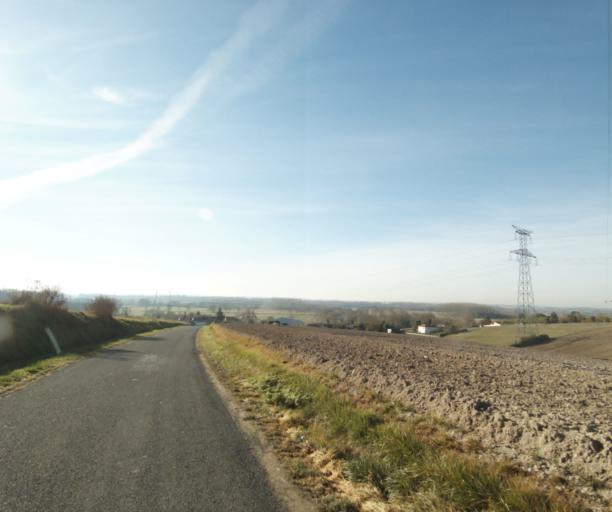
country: FR
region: Poitou-Charentes
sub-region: Departement de la Charente-Maritime
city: Chaniers
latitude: 45.7291
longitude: -0.5793
